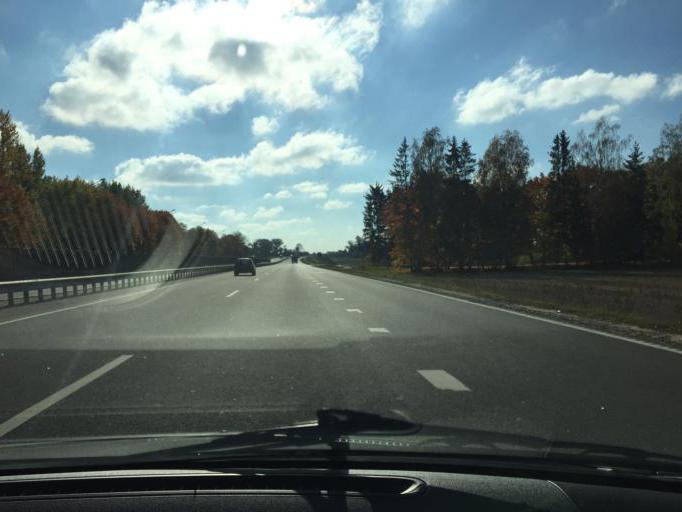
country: BY
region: Minsk
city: Slutsk
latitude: 53.0900
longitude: 27.5697
